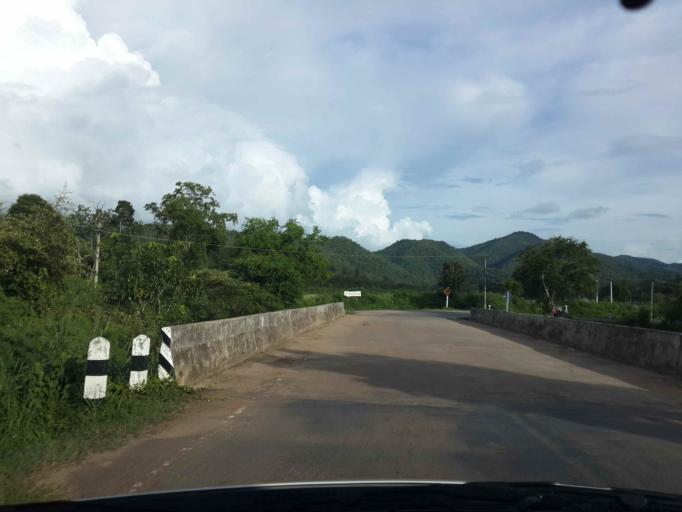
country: TH
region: Kanchanaburi
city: Sai Yok
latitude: 13.8801
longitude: 99.1706
